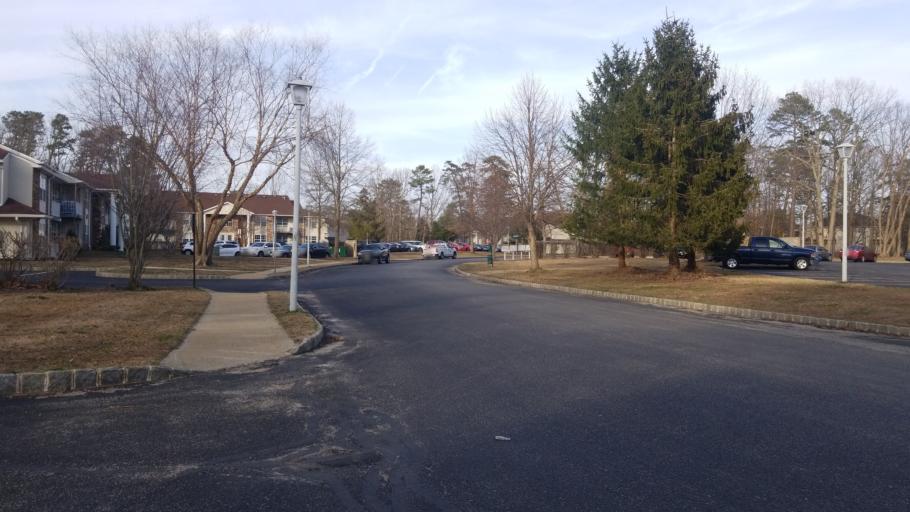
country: US
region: New Jersey
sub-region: Ocean County
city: Leisure Knoll
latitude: 39.9986
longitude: -74.2927
